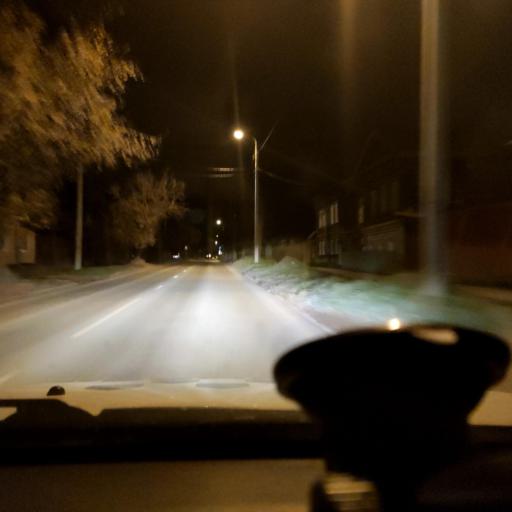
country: RU
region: Perm
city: Perm
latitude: 58.0300
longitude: 56.3283
